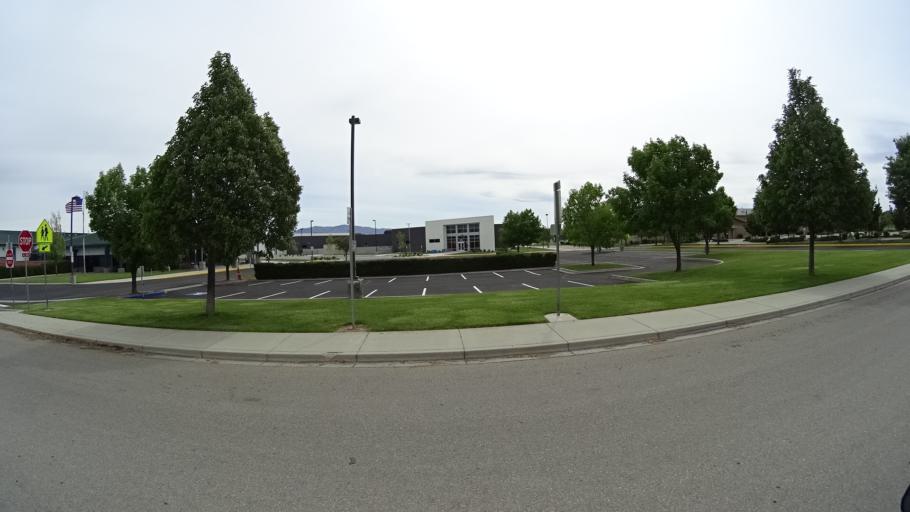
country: US
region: Idaho
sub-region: Ada County
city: Garden City
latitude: 43.5717
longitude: -116.2840
